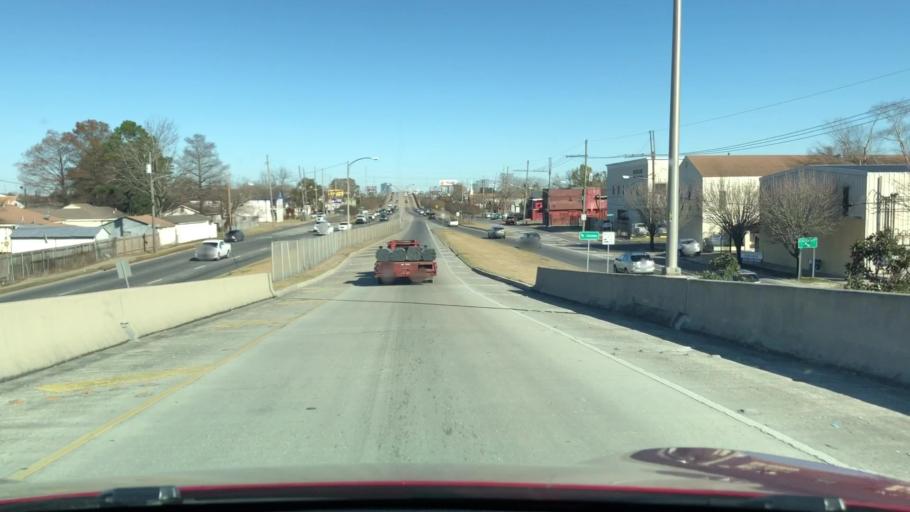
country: US
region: Louisiana
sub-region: Jefferson Parish
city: Jefferson
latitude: 29.9637
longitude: -90.1568
